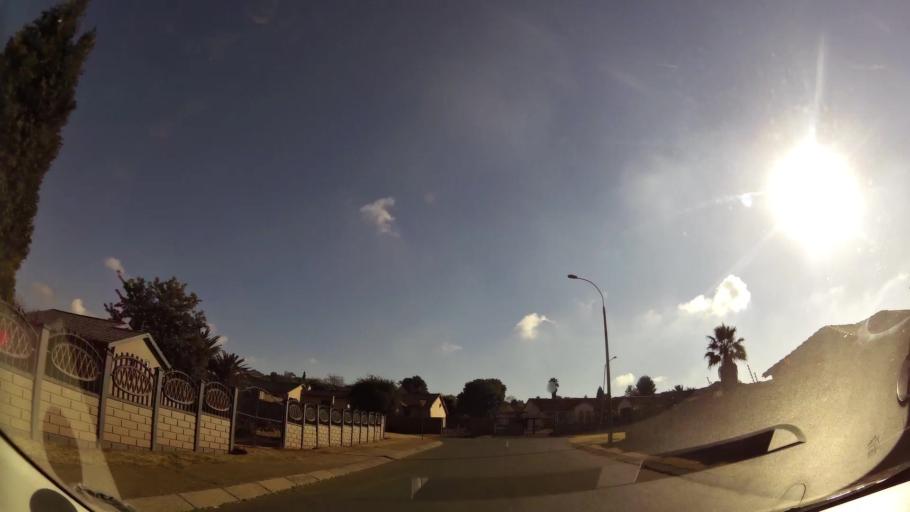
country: ZA
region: Gauteng
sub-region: City of Johannesburg Metropolitan Municipality
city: Roodepoort
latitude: -26.1527
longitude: 27.8426
